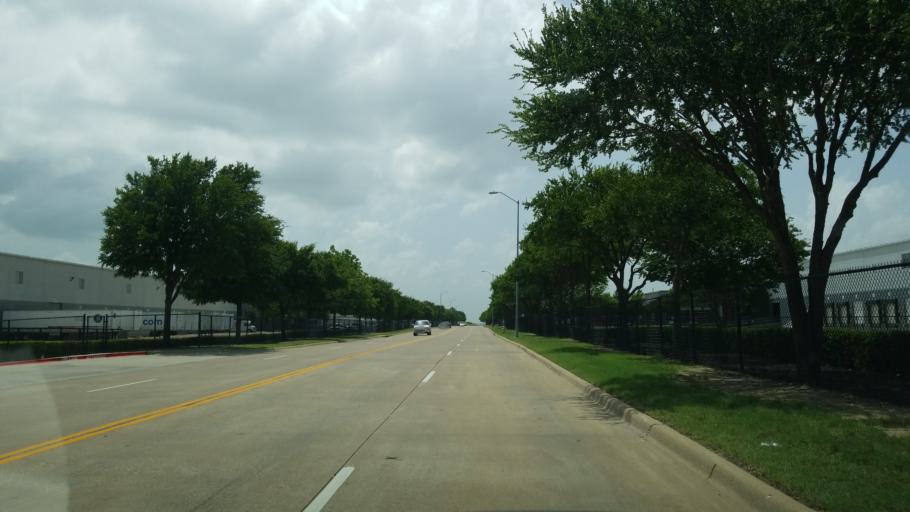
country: US
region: Texas
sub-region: Dallas County
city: Cockrell Hill
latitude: 32.7599
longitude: -96.8819
